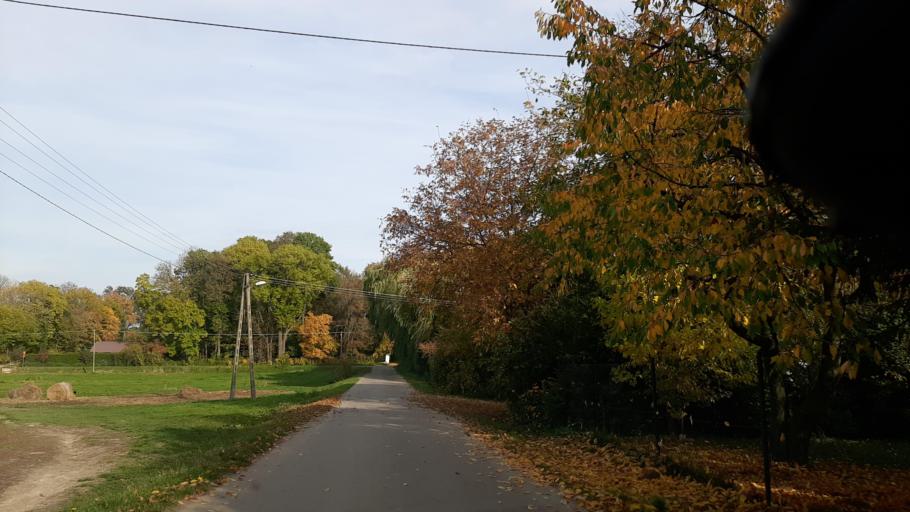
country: PL
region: Lublin Voivodeship
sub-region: Powiat lubelski
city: Jastkow
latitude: 51.3416
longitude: 22.4107
